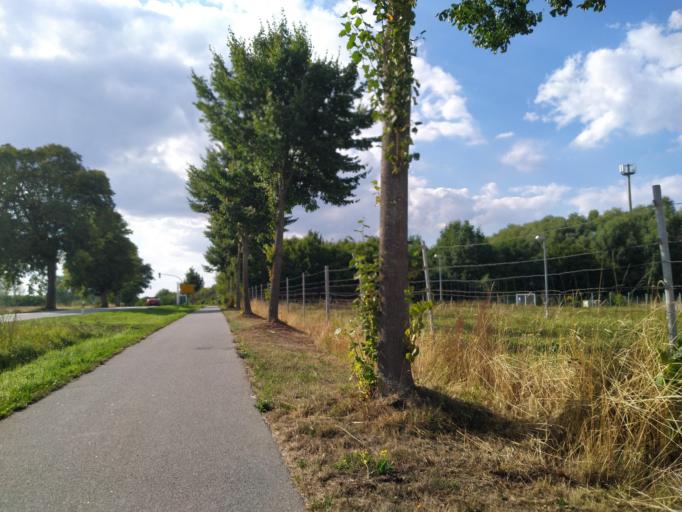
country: DE
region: Mecklenburg-Vorpommern
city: Wismar
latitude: 53.9010
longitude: 11.4061
